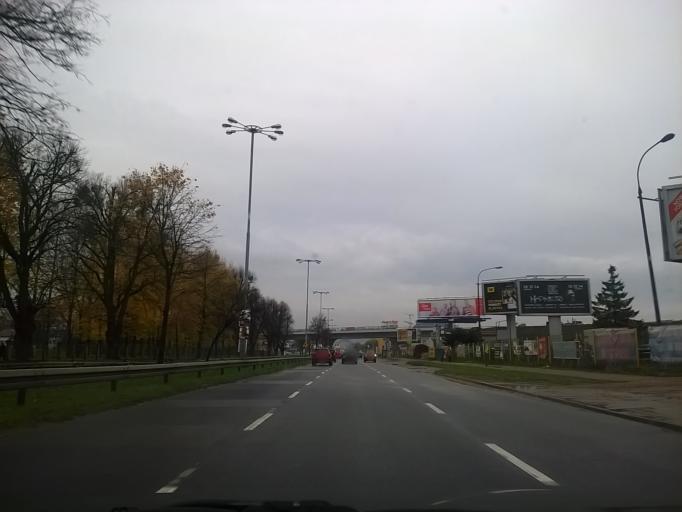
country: PL
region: Pomeranian Voivodeship
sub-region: Sopot
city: Sopot
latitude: 54.3913
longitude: 18.5854
